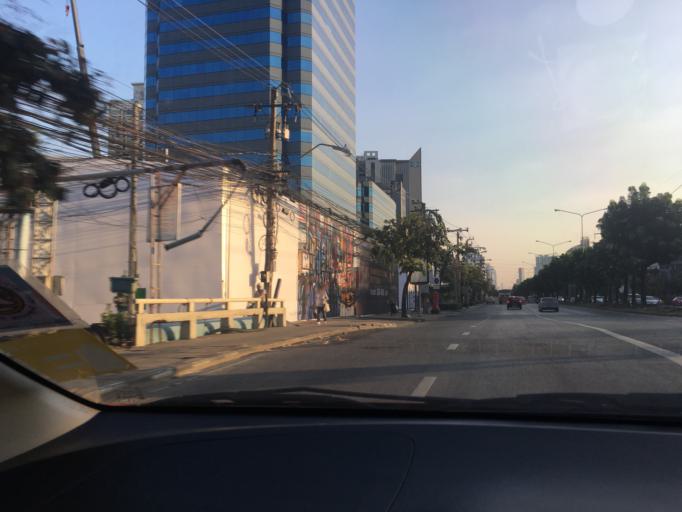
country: TH
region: Bangkok
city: Huai Khwang
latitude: 13.8014
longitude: 100.5748
